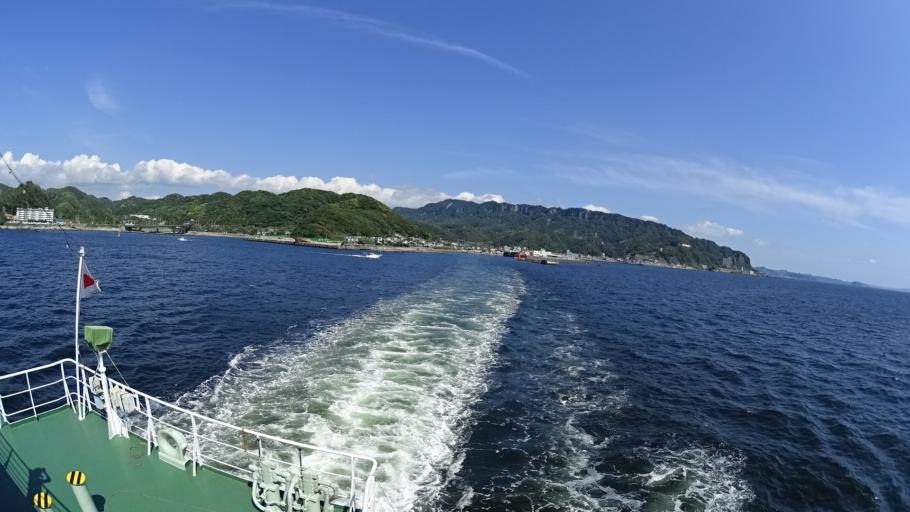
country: JP
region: Chiba
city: Futtsu
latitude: 35.1731
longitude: 139.8121
